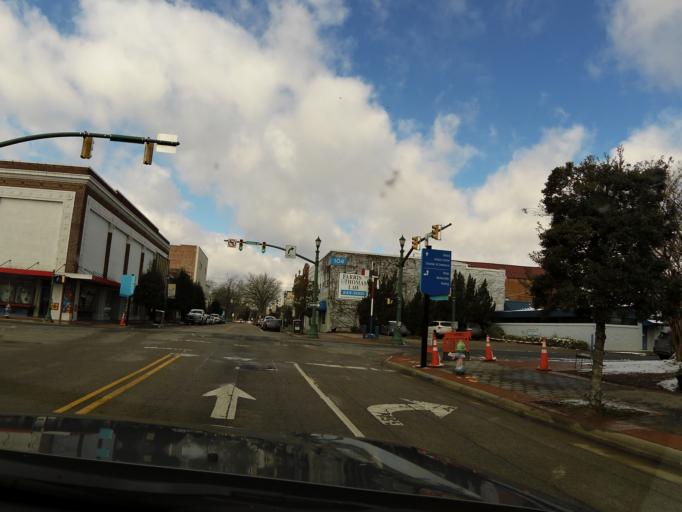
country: US
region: North Carolina
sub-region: Wilson County
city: Wilson
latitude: 35.7255
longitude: -77.9108
